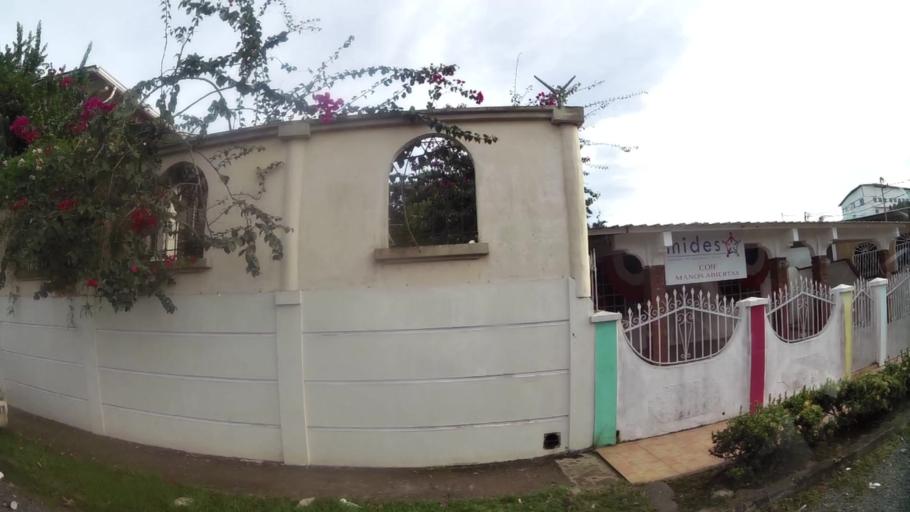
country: PA
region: Panama
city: La Chorrera
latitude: 8.8912
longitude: -79.7695
